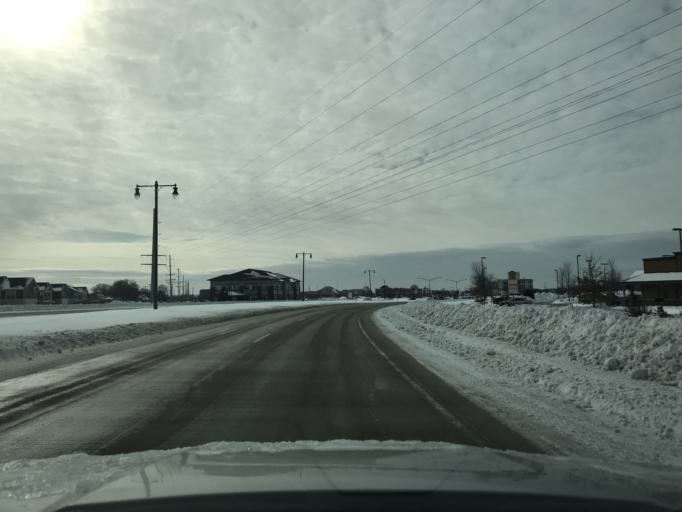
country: US
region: Wisconsin
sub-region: Dane County
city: Sun Prairie
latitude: 43.1712
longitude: -89.2653
